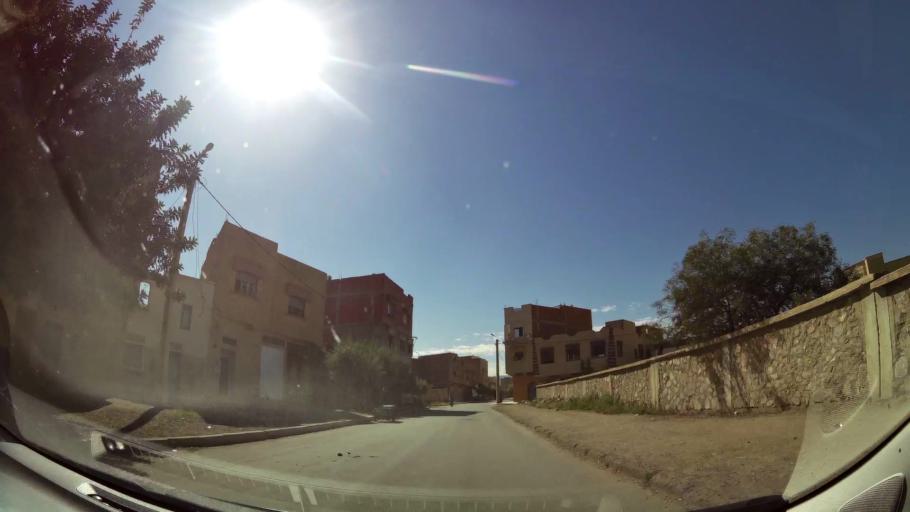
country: MA
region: Oriental
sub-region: Oujda-Angad
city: Oujda
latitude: 34.6643
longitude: -1.8873
